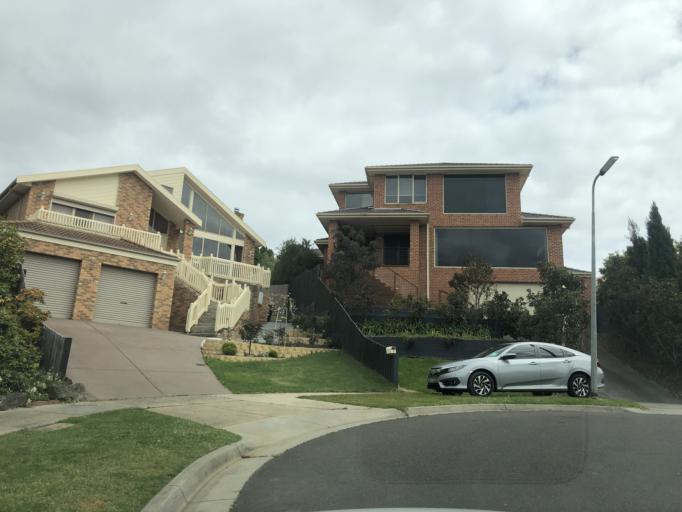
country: AU
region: Victoria
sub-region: Greater Dandenong
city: Noble Park North
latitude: -37.9370
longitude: 145.2107
